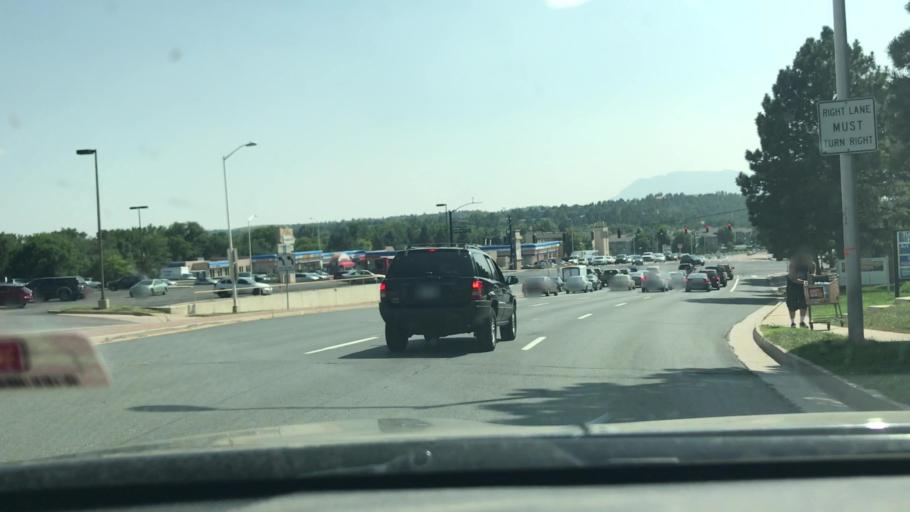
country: US
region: Colorado
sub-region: El Paso County
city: Colorado Springs
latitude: 38.9056
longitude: -104.7751
